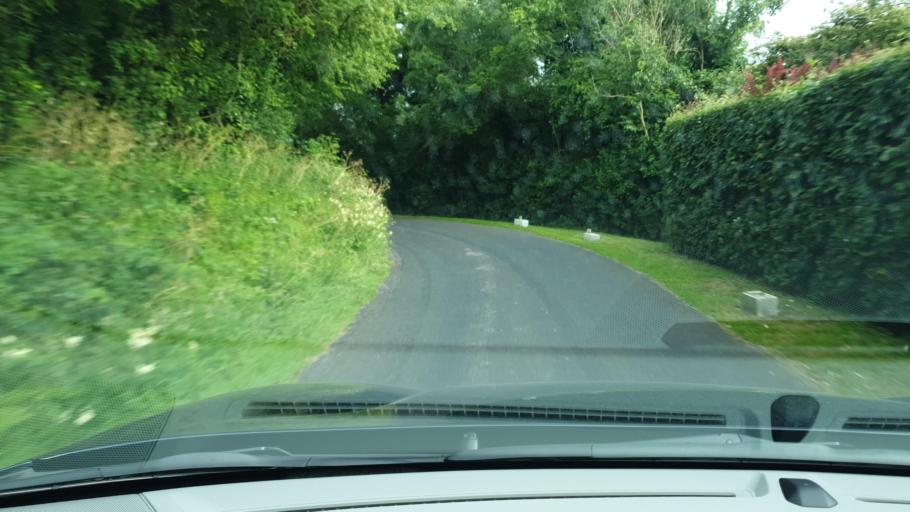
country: IE
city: Confey
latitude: 53.4016
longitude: -6.5092
